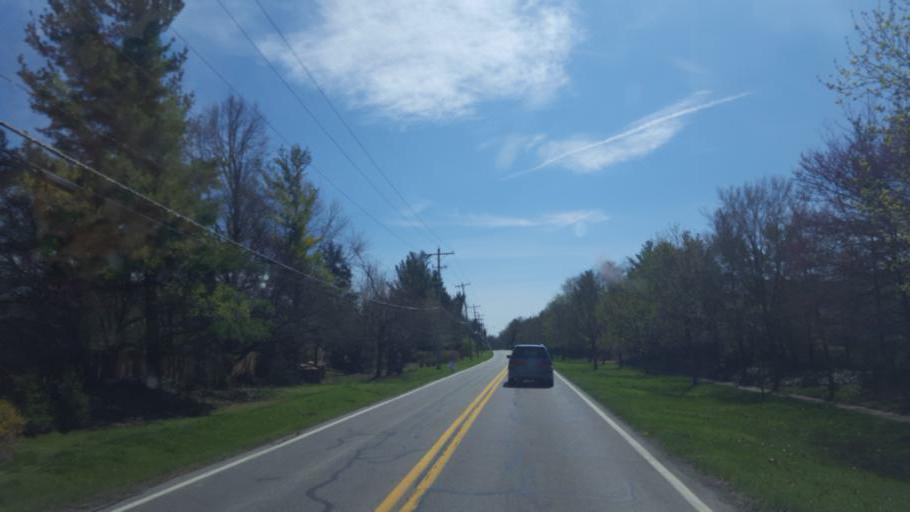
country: US
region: Ohio
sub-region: Franklin County
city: Worthington
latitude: 40.1016
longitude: -83.0466
